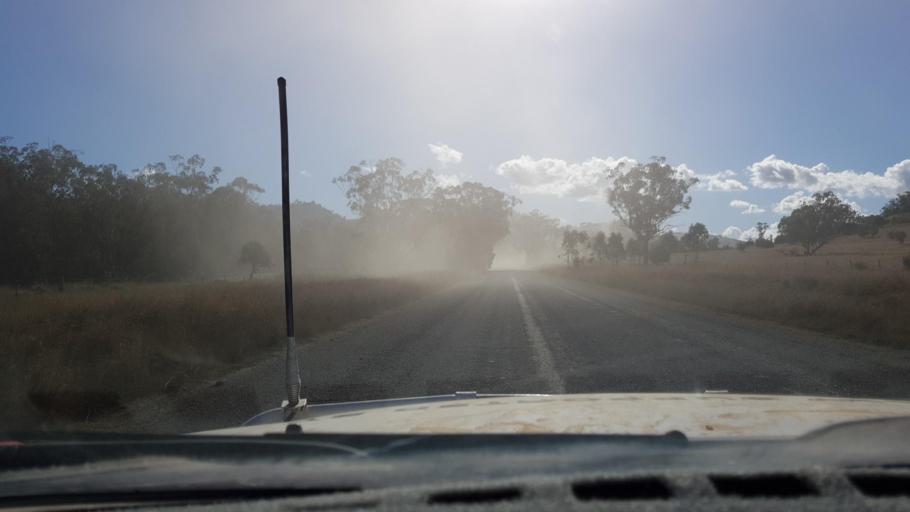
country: AU
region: New South Wales
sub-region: Narrabri
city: Blair Athol
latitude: -30.6679
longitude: 150.3441
